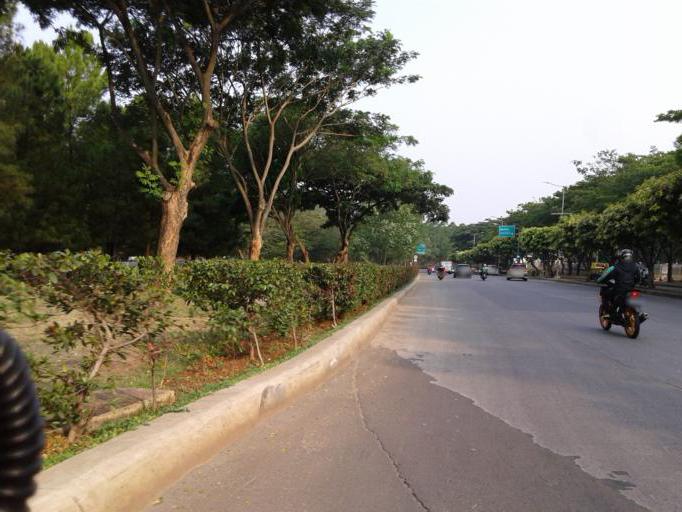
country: ID
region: Banten
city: South Tangerang
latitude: -6.2827
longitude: 106.7287
